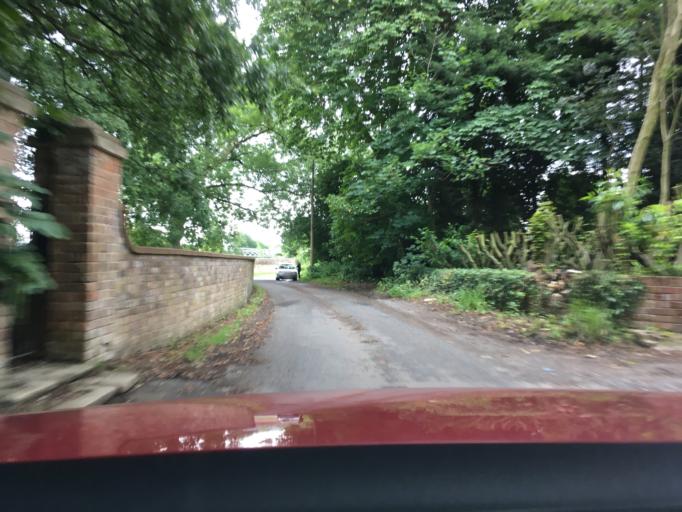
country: GB
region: England
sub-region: Gloucestershire
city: Dursley
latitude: 51.7820
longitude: -2.3872
